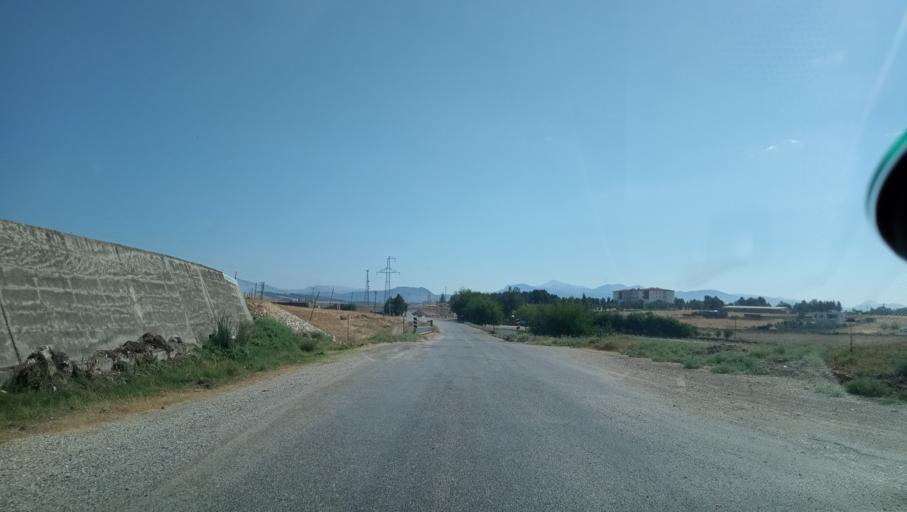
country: TR
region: Diyarbakir
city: Malabadi
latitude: 38.1345
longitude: 41.1886
